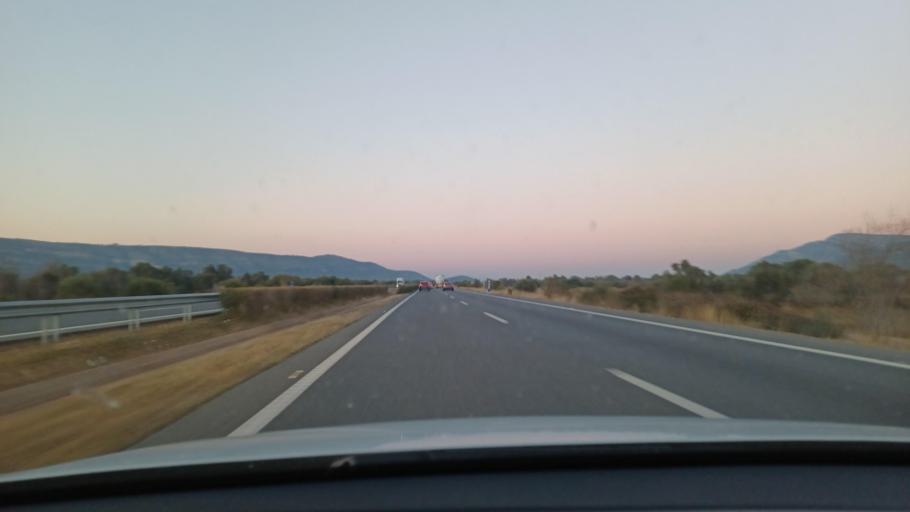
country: ES
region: Catalonia
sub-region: Provincia de Tarragona
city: Ulldecona
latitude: 40.6035
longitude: 0.4735
